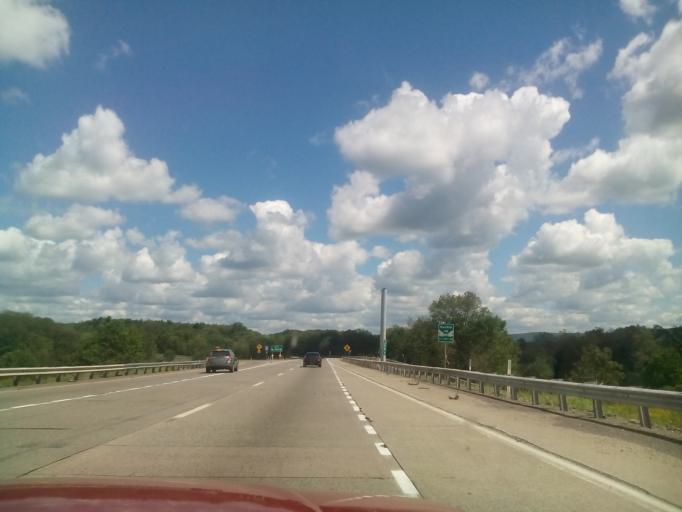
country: US
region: Pennsylvania
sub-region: Luzerne County
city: Conyngham
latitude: 41.0453
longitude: -76.0136
